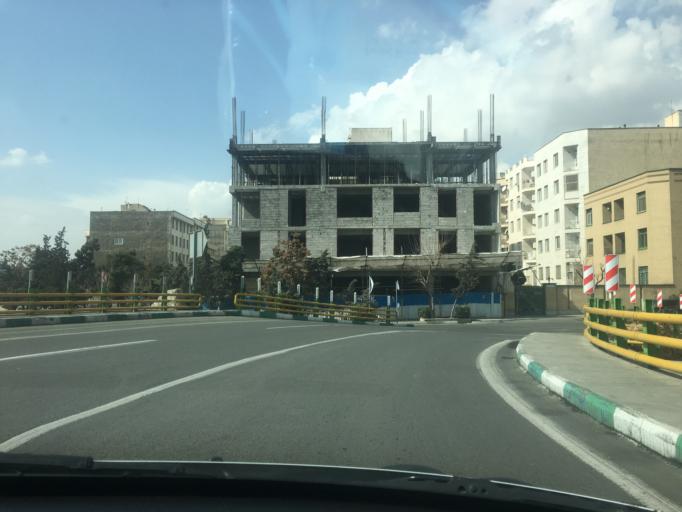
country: IR
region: Tehran
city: Tehran
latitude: 35.7177
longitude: 51.3224
